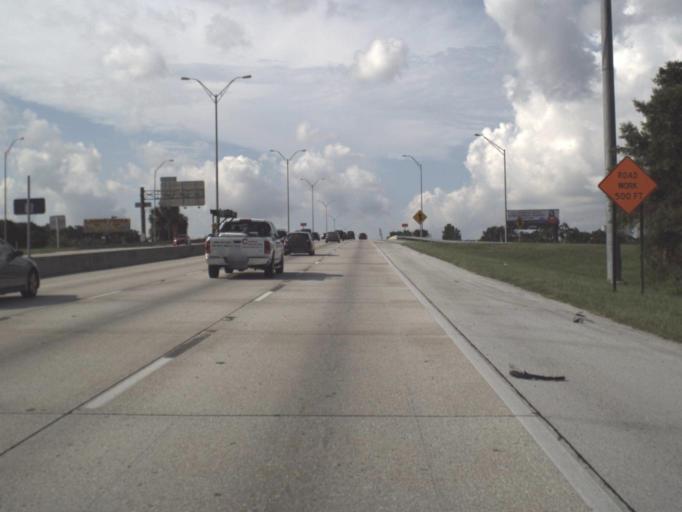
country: US
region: Florida
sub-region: Hillsborough County
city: University
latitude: 28.0351
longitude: -82.4551
